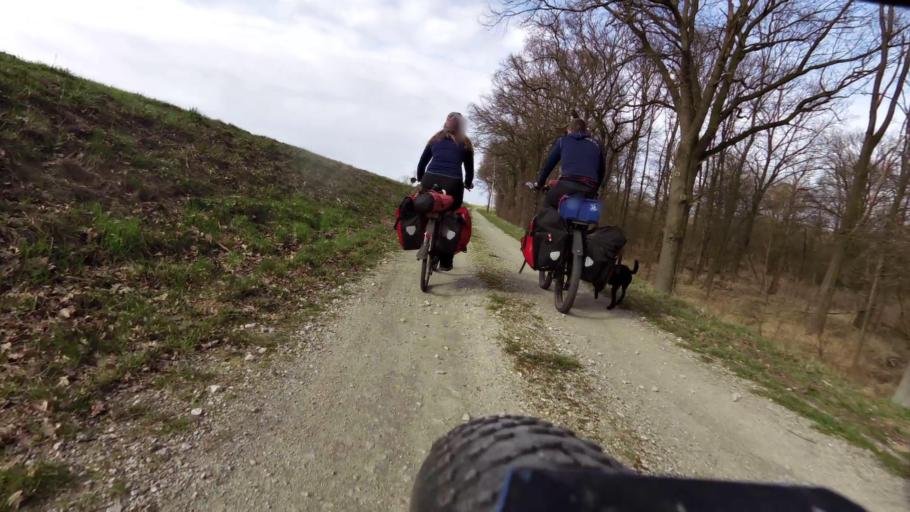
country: DE
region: Brandenburg
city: Reitwein
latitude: 52.5228
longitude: 14.6108
